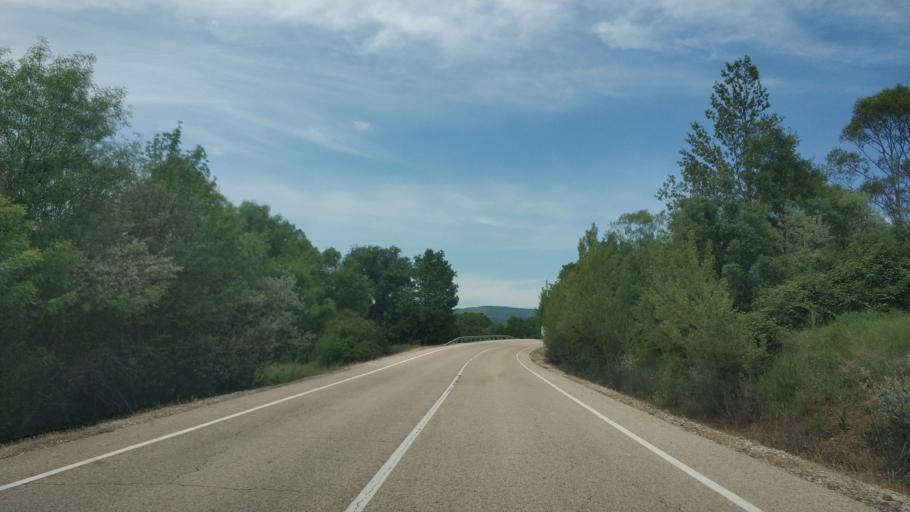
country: ES
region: Castille and Leon
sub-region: Provincia de Soria
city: Sotillo del Rincon
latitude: 41.8868
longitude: -2.6218
